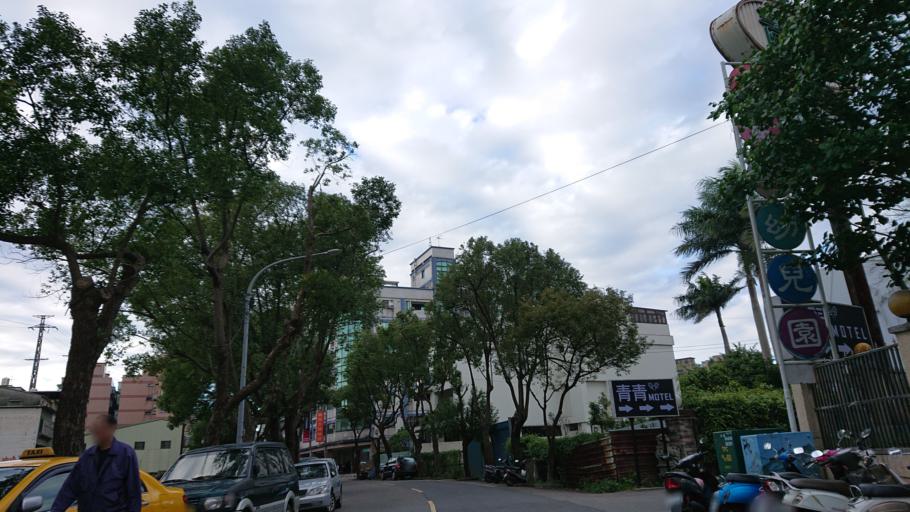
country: TW
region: Taiwan
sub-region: Taoyuan
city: Taoyuan
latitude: 24.9318
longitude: 121.3788
